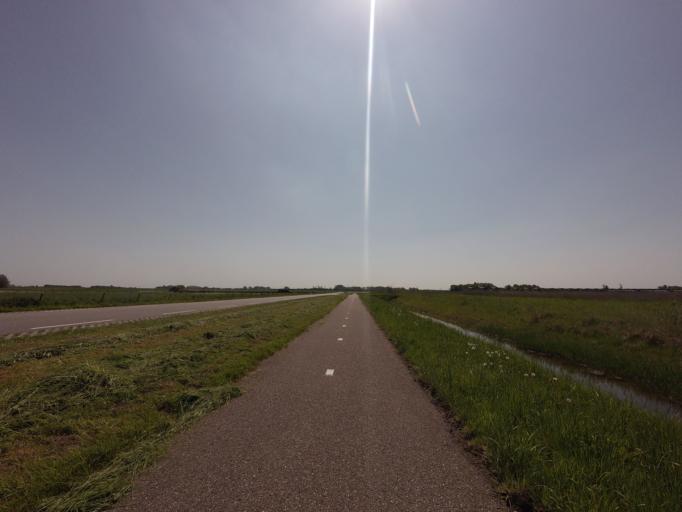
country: NL
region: Zeeland
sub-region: Gemeente Noord-Beveland
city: Kamperland
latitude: 51.5122
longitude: 3.7211
